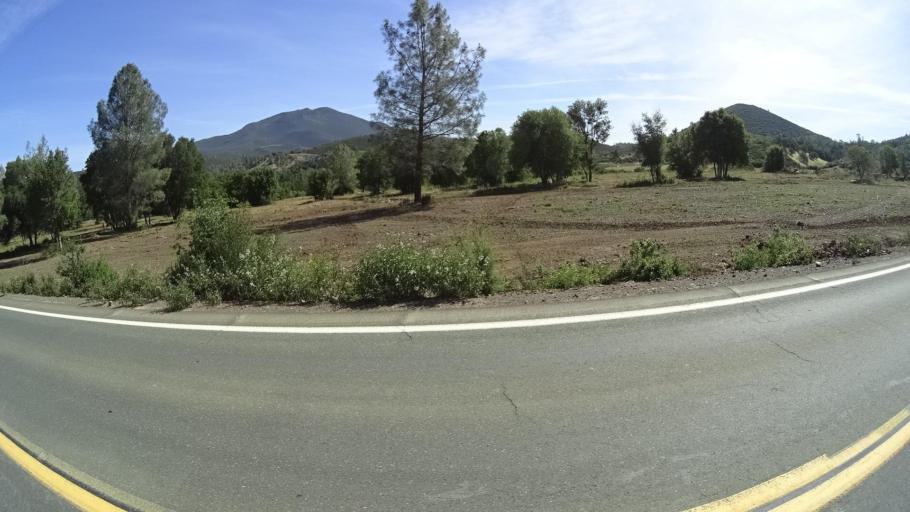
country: US
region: California
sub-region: Lake County
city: Kelseyville
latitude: 38.9327
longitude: -122.8099
